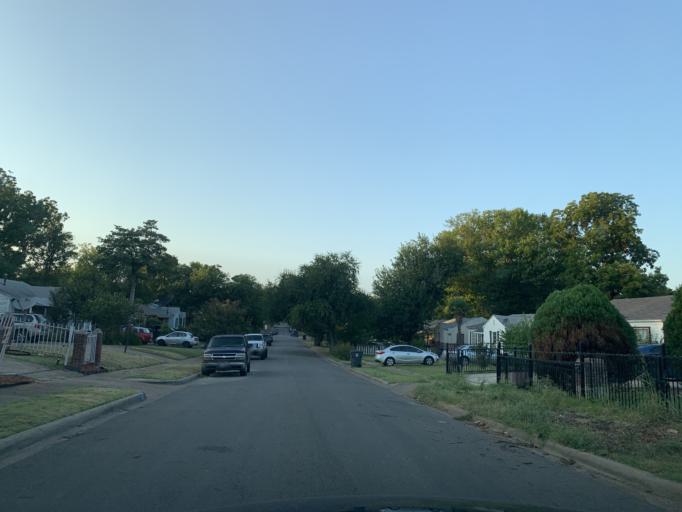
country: US
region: Texas
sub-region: Dallas County
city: Dallas
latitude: 32.7063
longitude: -96.8095
